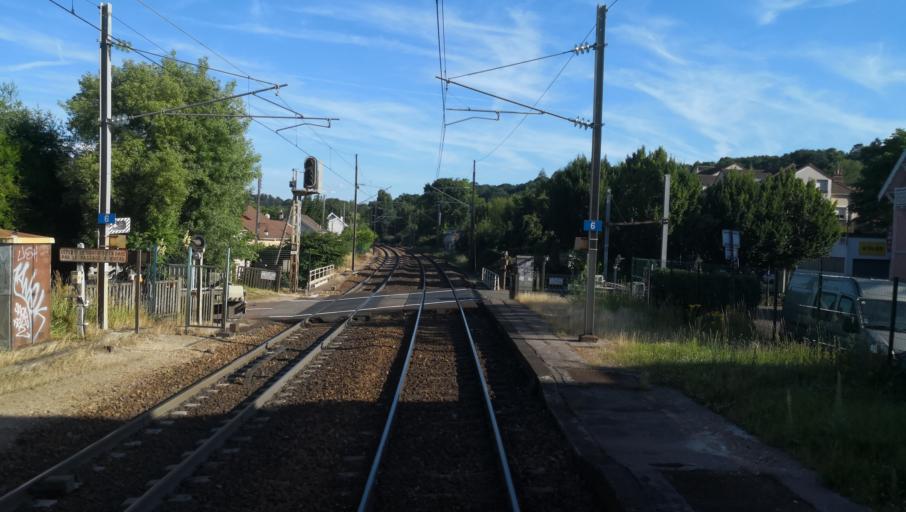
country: FR
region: Ile-de-France
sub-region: Departement des Yvelines
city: Villennes-sur-Seine
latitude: 48.9381
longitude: 1.9997
